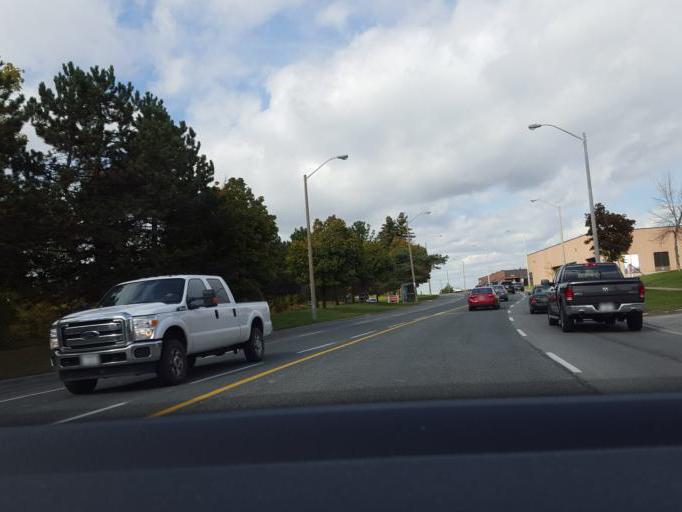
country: CA
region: Ontario
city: Scarborough
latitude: 43.8027
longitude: -79.2000
